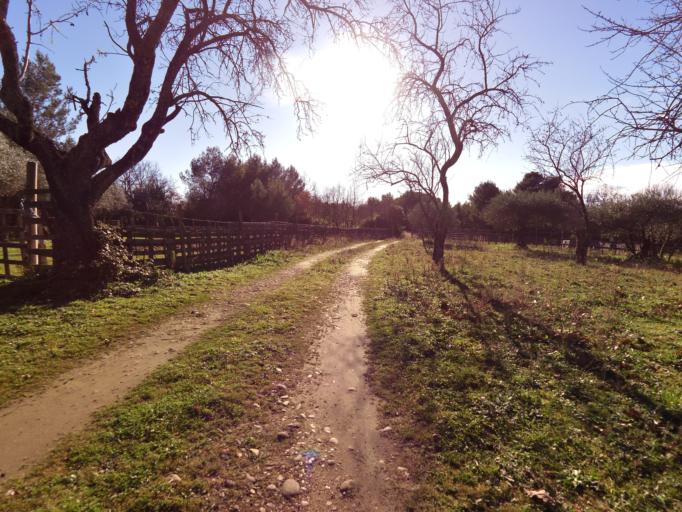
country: FR
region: Languedoc-Roussillon
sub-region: Departement du Gard
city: Mus
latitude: 43.7381
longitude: 4.1920
